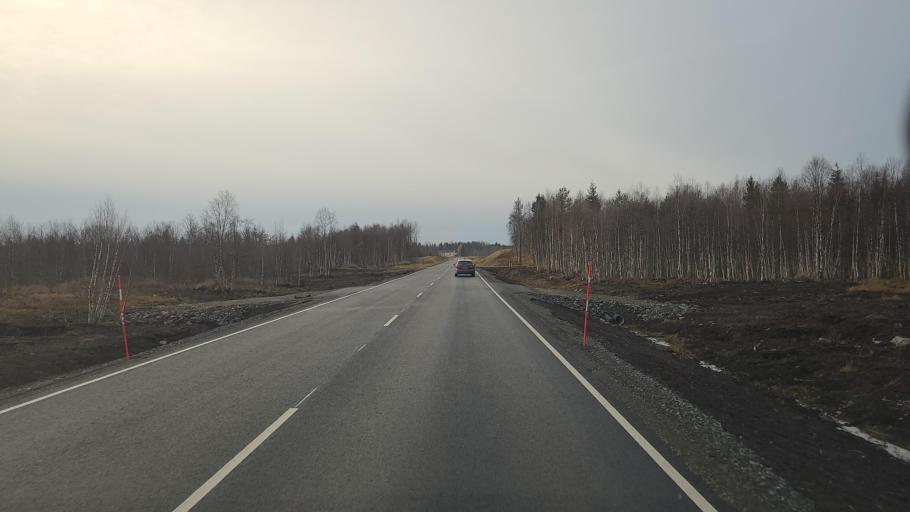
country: FI
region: Lapland
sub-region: Tunturi-Lappi
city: Kittilae
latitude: 67.8648
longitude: 24.9589
